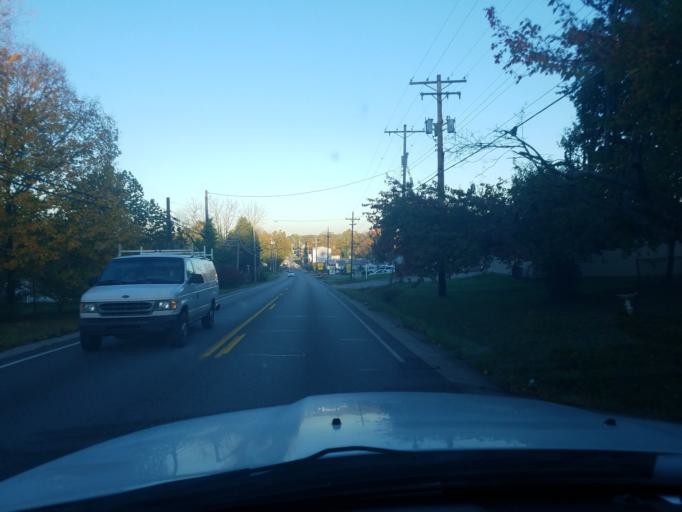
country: US
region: Indiana
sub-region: Floyd County
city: Galena
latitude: 38.3721
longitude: -85.9855
